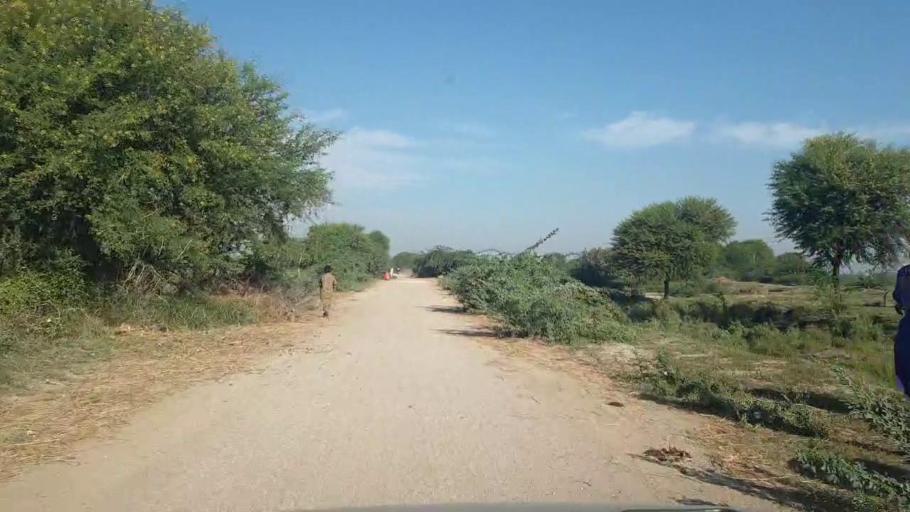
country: PK
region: Sindh
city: Talhar
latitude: 24.9410
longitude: 68.7888
